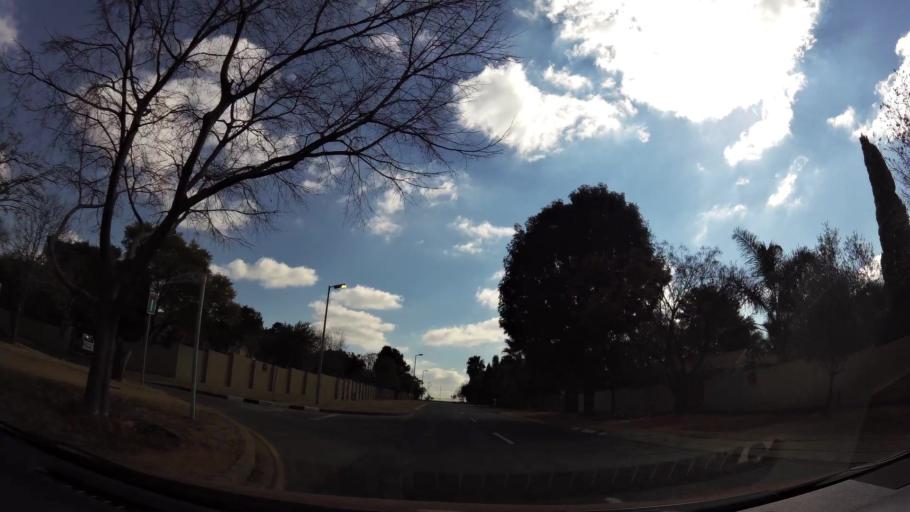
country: ZA
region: Gauteng
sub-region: City of Johannesburg Metropolitan Municipality
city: Roodepoort
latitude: -26.0835
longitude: 27.9353
